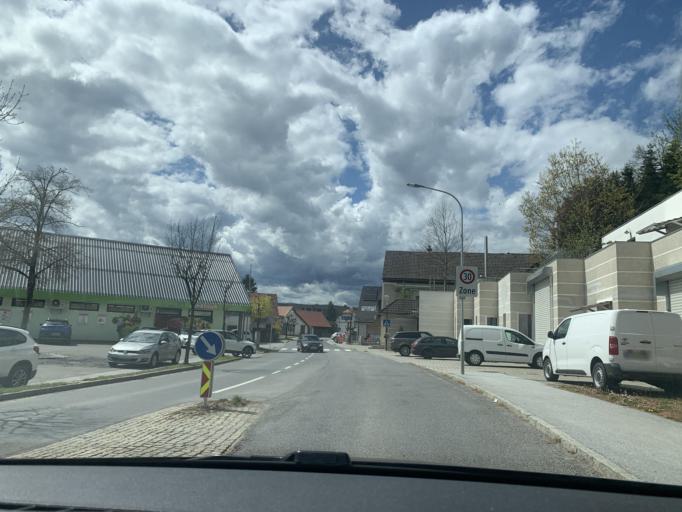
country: AT
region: Styria
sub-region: Politischer Bezirk Graz-Umgebung
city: Unterpremstatten
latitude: 46.9466
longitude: 15.3787
